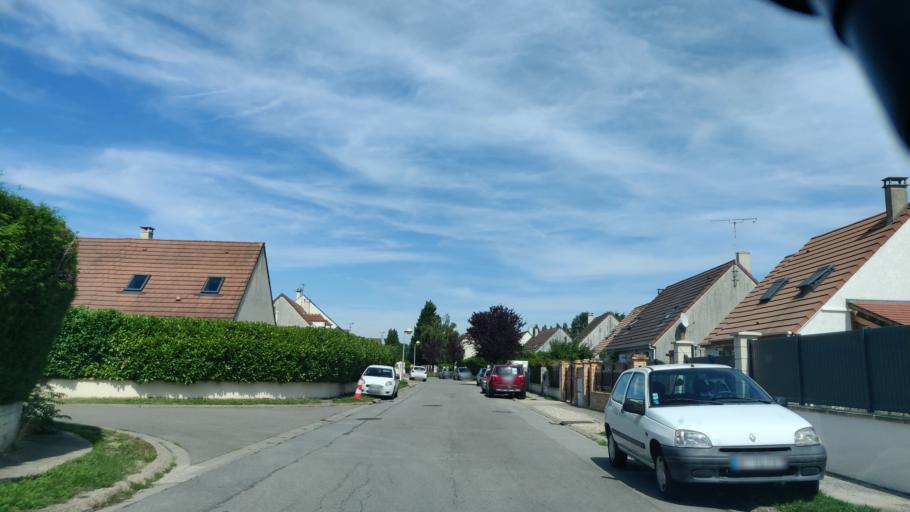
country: FR
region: Picardie
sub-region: Departement de l'Oise
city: Pont-Sainte-Maxence
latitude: 49.3123
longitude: 2.6203
